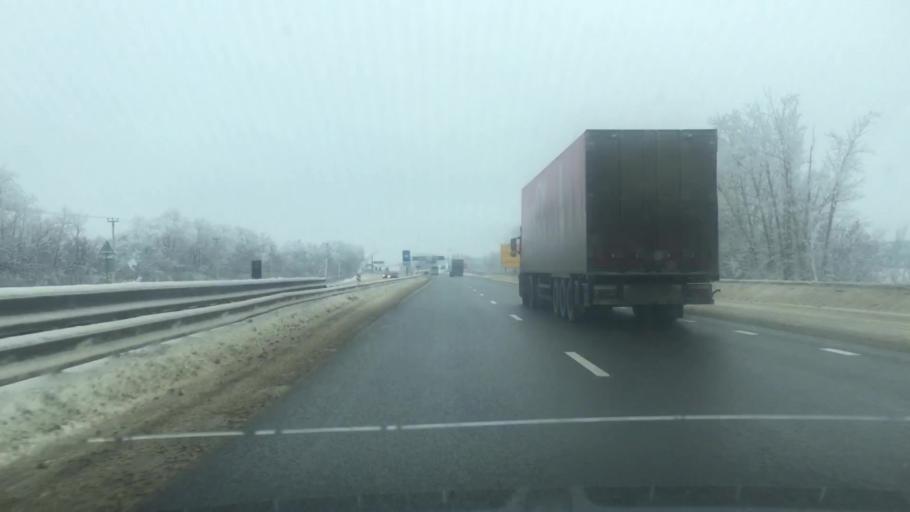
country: RU
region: Tula
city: Kazachka
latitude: 53.2988
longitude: 38.1781
